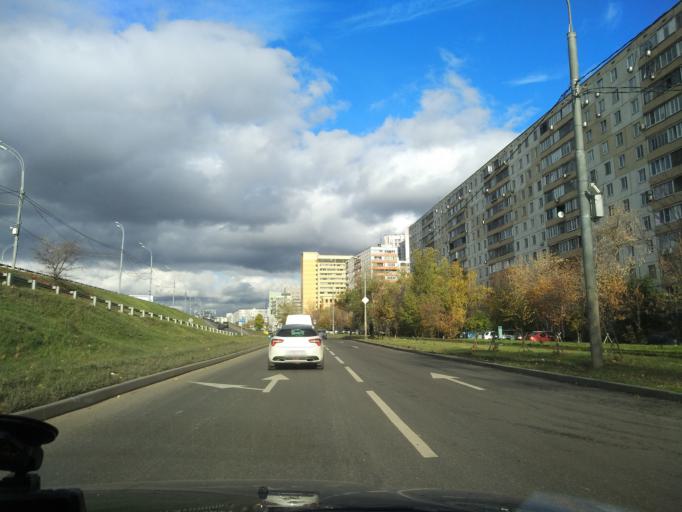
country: RU
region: Moscow
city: Slobodka
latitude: 55.8713
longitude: 37.5863
